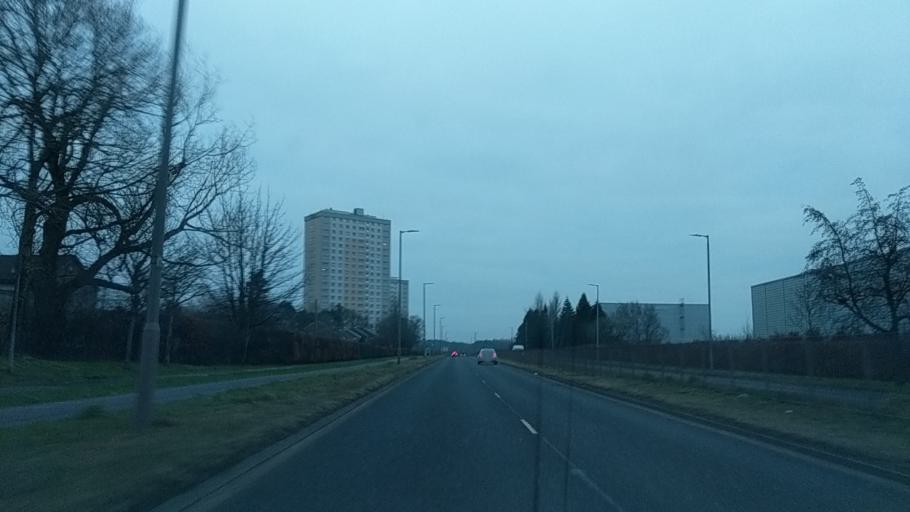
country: GB
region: Scotland
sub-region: South Lanarkshire
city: East Kilbride
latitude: 55.7567
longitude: -4.1625
